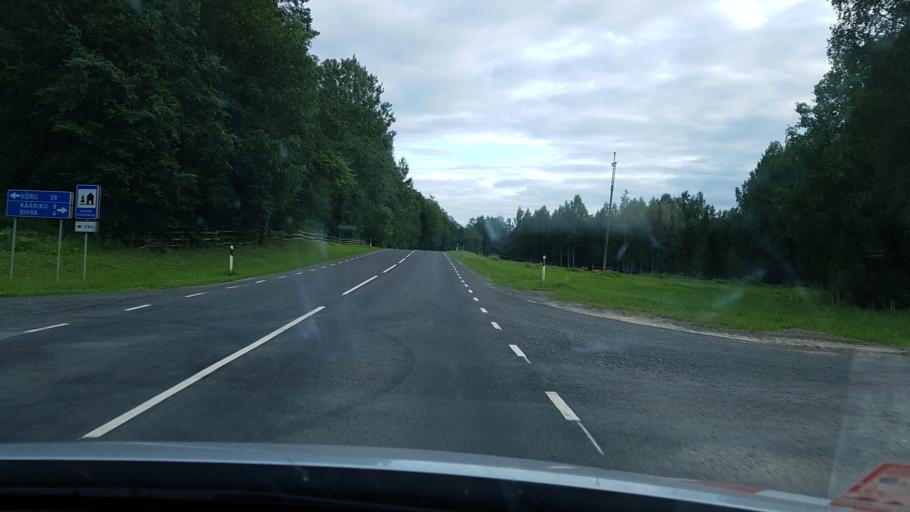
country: EE
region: Vorumaa
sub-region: Antsla vald
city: Vana-Antsla
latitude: 57.9968
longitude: 26.4952
